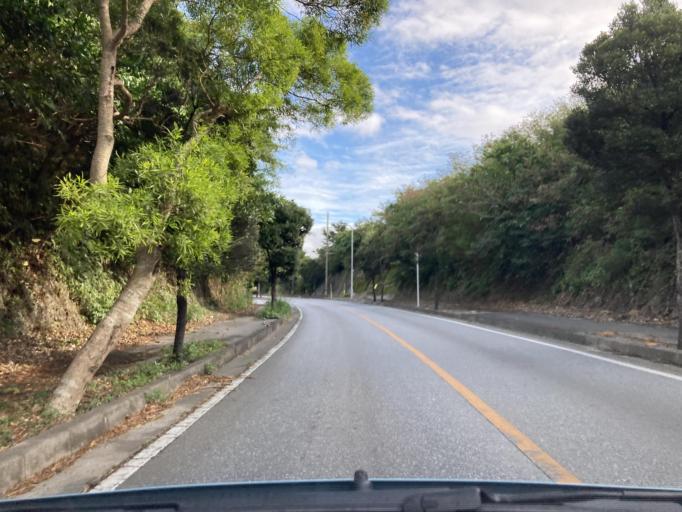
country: JP
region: Okinawa
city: Itoman
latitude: 26.1278
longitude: 127.7111
